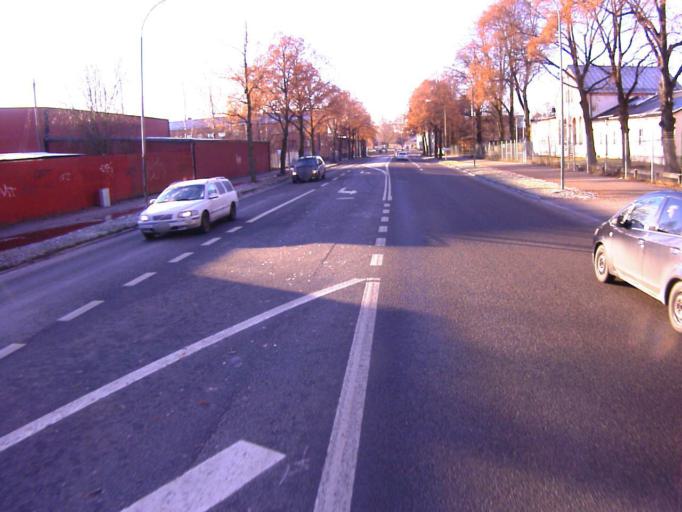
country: SE
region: Soedermanland
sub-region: Eskilstuna Kommun
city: Eskilstuna
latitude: 59.3805
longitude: 16.4975
